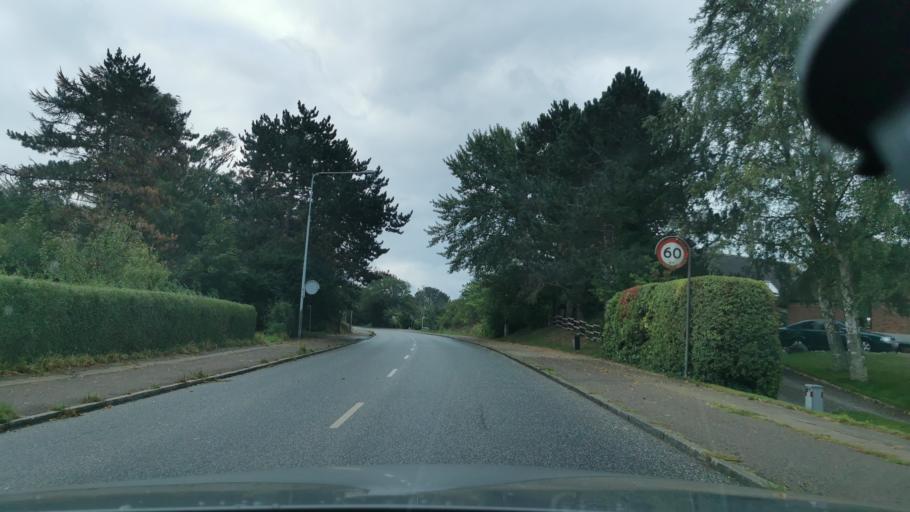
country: DK
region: Zealand
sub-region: Kalundborg Kommune
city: Kalundborg
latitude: 55.7036
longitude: 11.0245
